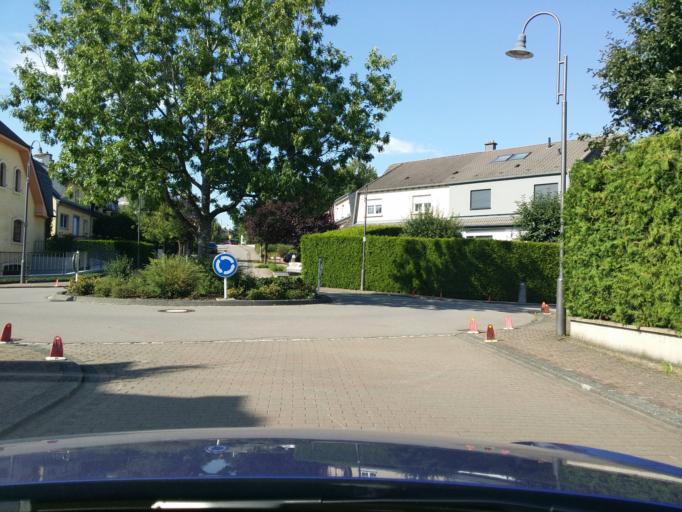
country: LU
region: Luxembourg
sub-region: Canton de Luxembourg
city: Bertrange
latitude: 49.6170
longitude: 6.0585
